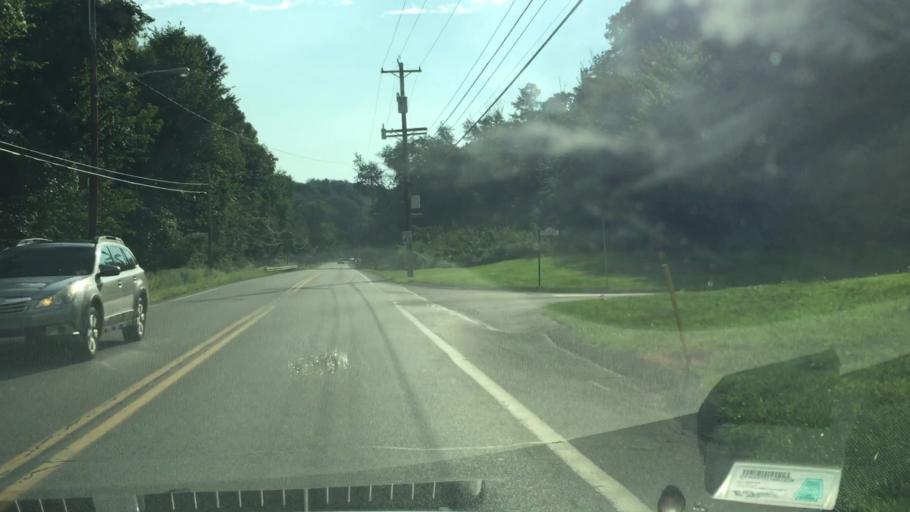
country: US
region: Pennsylvania
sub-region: Allegheny County
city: Carnot-Moon
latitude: 40.5261
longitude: -80.2506
